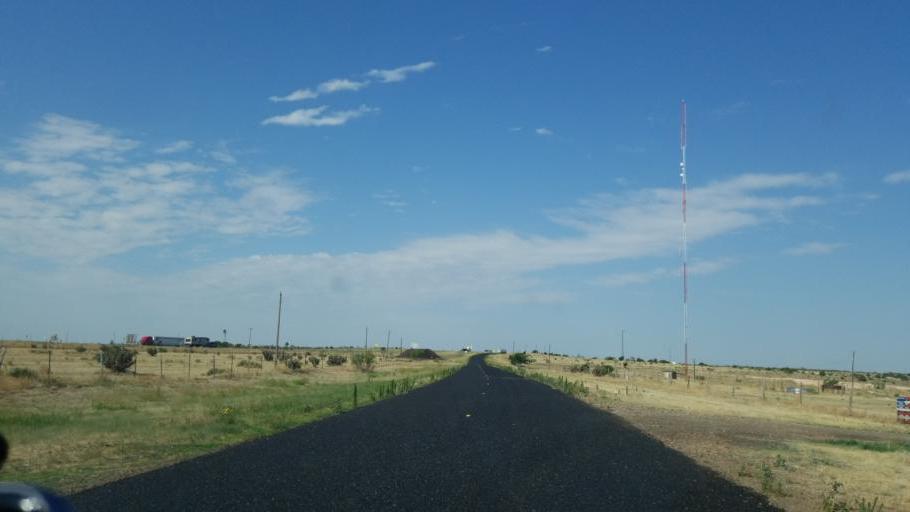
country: US
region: Texas
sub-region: Oldham County
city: Vega
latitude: 35.2601
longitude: -102.7598
